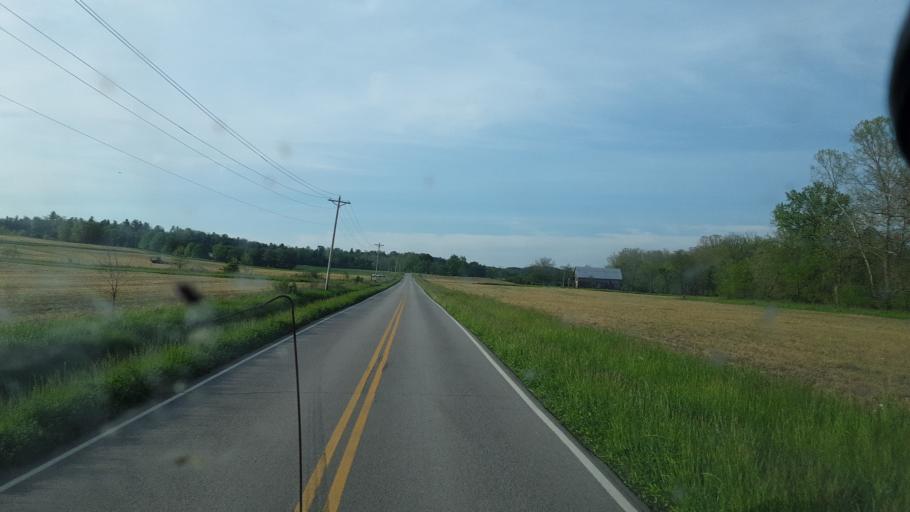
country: US
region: Ohio
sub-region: Ross County
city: Kingston
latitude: 39.5028
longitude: -82.6996
